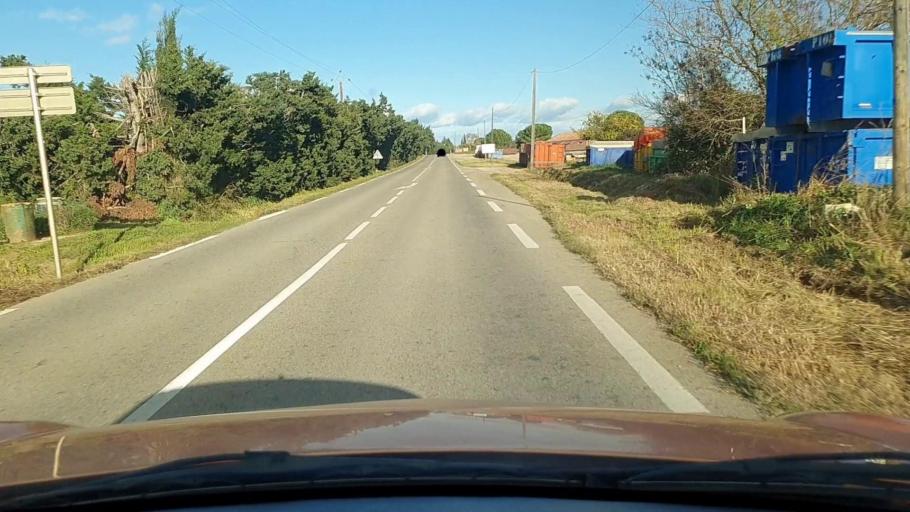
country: FR
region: Languedoc-Roussillon
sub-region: Departement du Gard
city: Generac
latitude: 43.6619
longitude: 4.3631
